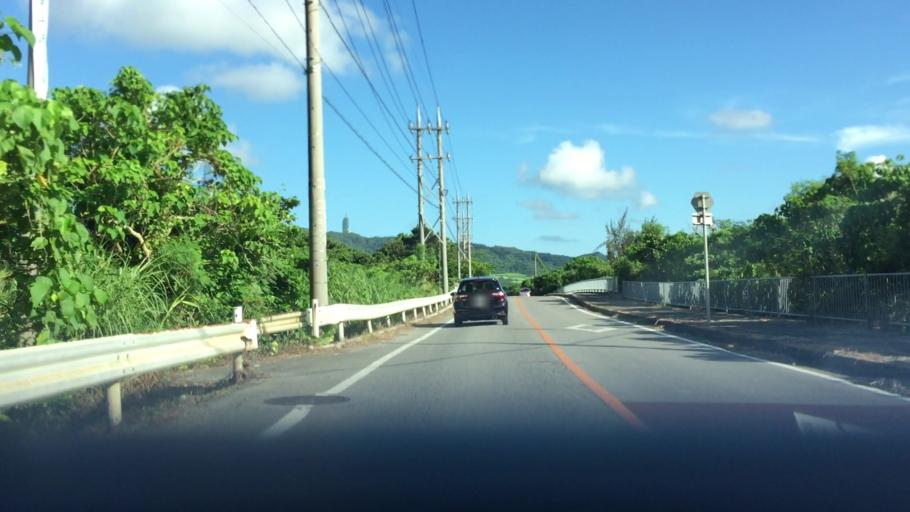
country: JP
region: Okinawa
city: Ishigaki
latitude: 24.4025
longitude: 124.1494
